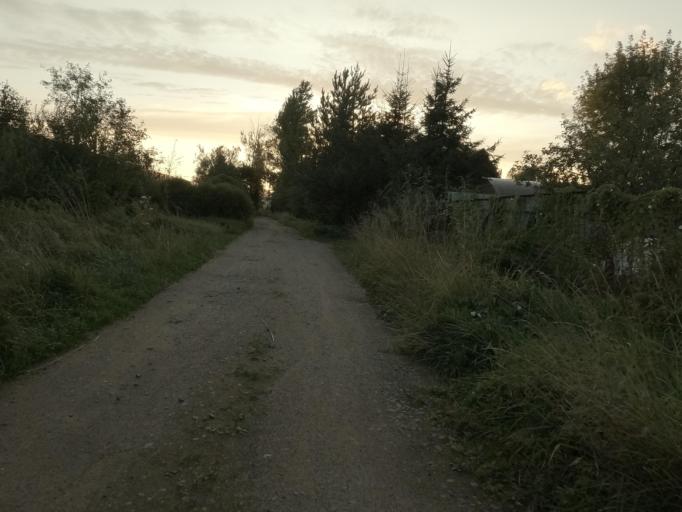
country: RU
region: Leningrad
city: Mga
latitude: 59.7579
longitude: 31.0449
